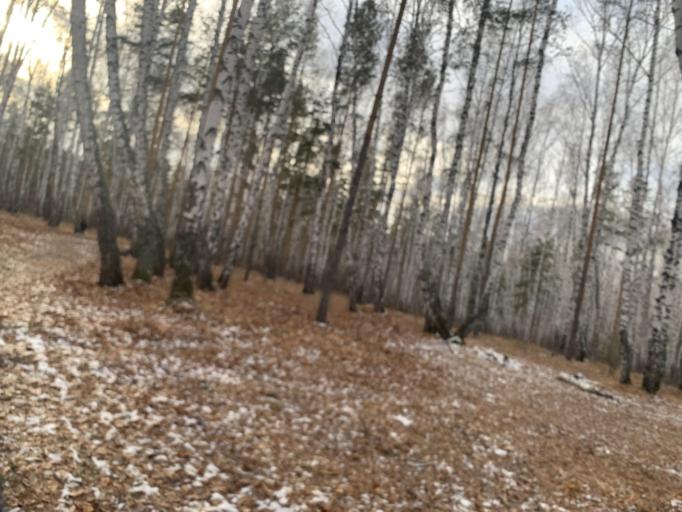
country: RU
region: Chelyabinsk
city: Roshchino
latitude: 55.2008
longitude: 61.3020
